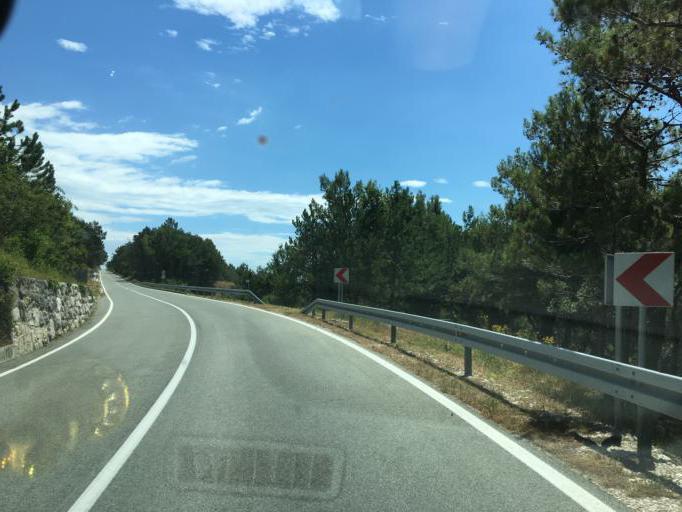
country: HR
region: Istarska
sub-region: Grad Labin
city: Rabac
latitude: 45.1269
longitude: 14.1959
